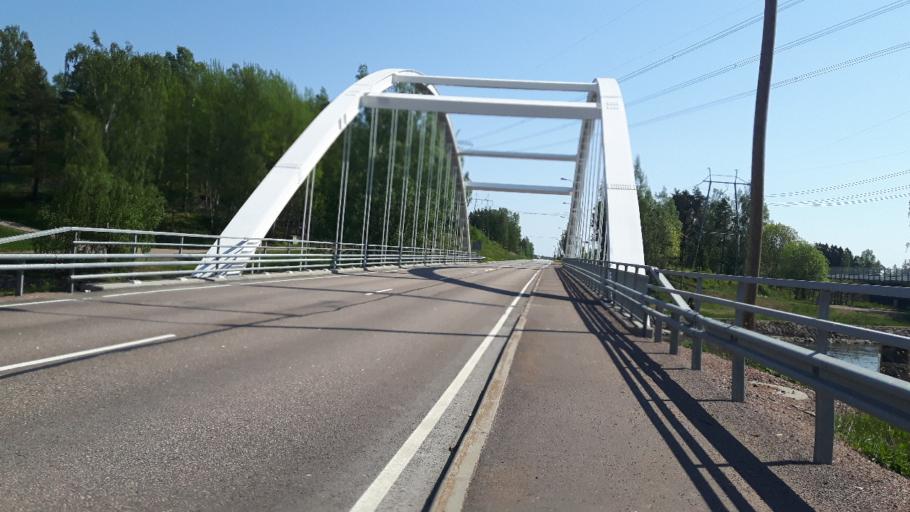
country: FI
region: Uusimaa
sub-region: Loviisa
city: Ruotsinpyhtaeae
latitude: 60.4932
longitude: 26.4504
